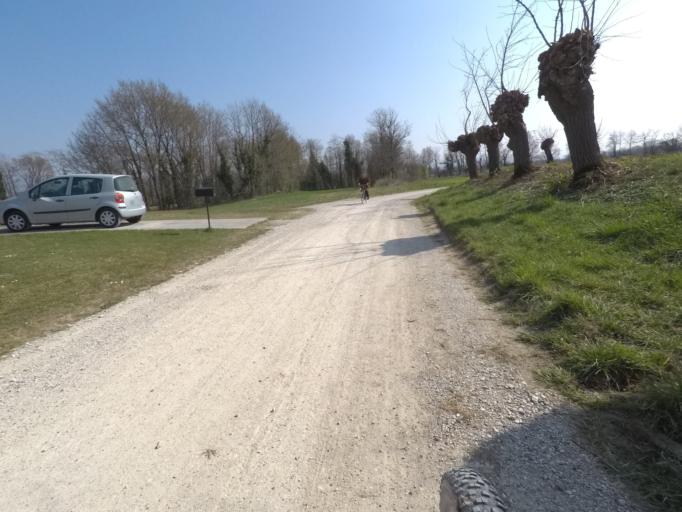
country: IT
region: Friuli Venezia Giulia
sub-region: Provincia di Udine
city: Remanzacco
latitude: 46.0810
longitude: 13.3289
